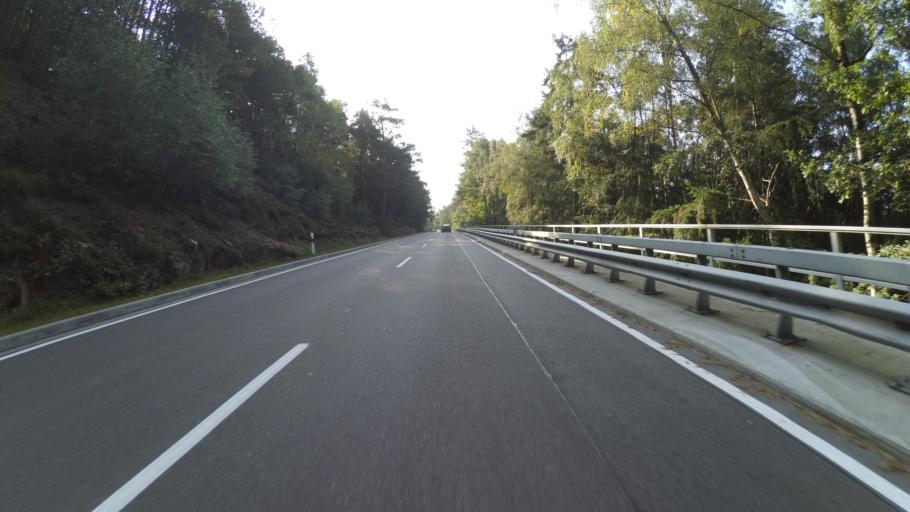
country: DE
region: Rheinland-Pfalz
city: Langwieden
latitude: 49.4008
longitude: 7.5199
